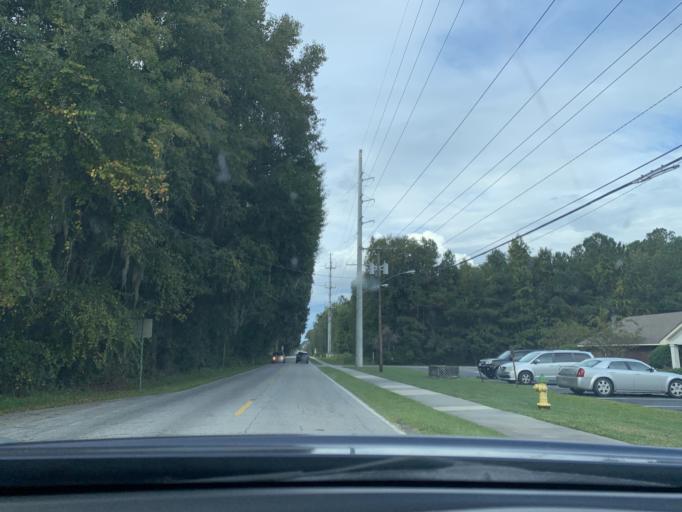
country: US
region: Georgia
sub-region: Chatham County
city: Pooler
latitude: 32.0952
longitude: -81.2562
